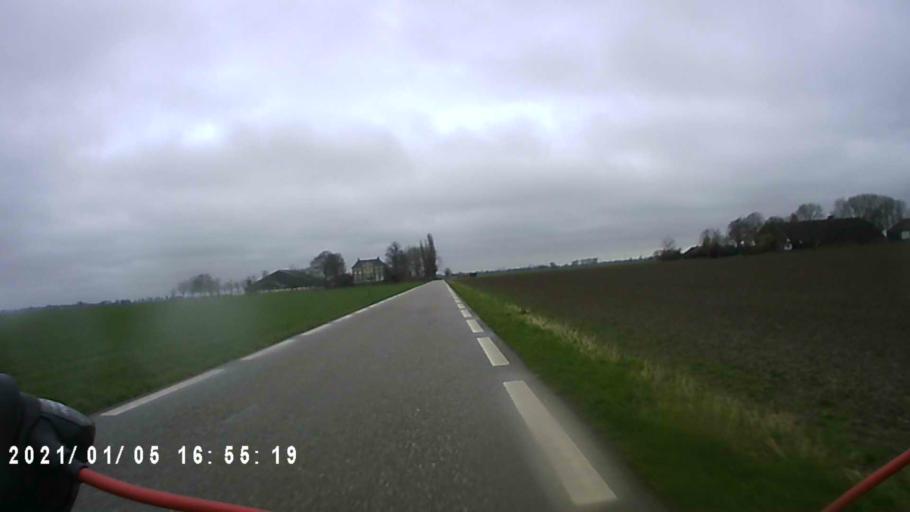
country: NL
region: Groningen
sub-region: Gemeente  Oldambt
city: Winschoten
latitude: 53.2432
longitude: 7.0547
